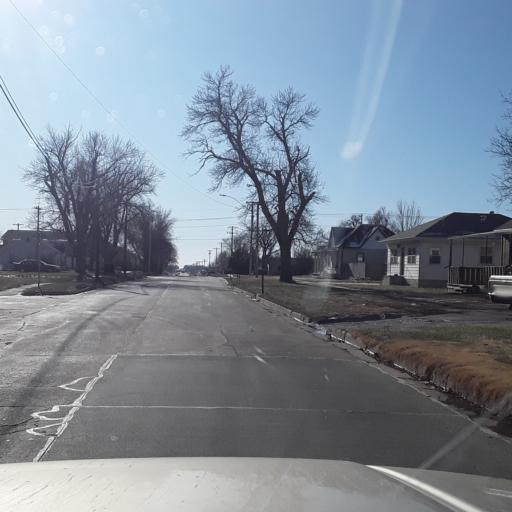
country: US
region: Nebraska
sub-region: Adams County
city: Hastings
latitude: 40.5783
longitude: -98.4021
